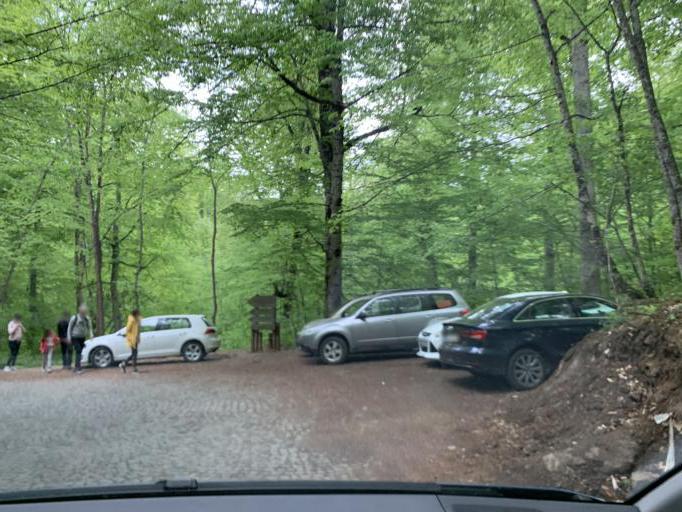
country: TR
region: Zonguldak
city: Egerci
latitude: 40.9385
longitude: 31.7435
